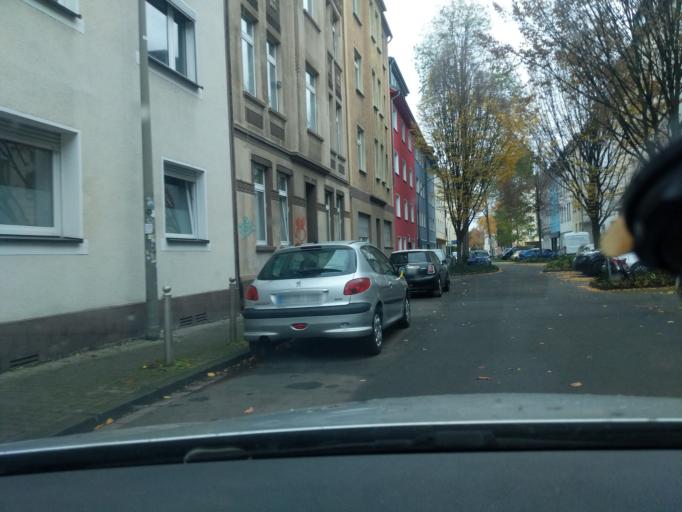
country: DE
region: North Rhine-Westphalia
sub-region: Regierungsbezirk Arnsberg
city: Dortmund
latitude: 51.5097
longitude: 7.4452
